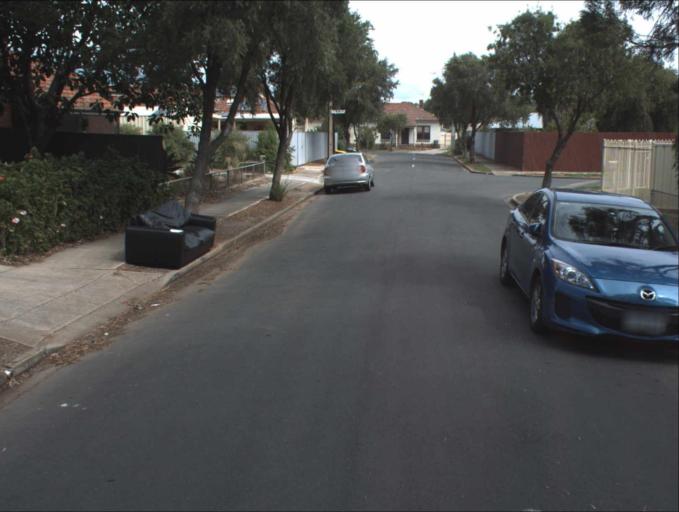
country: AU
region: South Australia
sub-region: Port Adelaide Enfield
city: Blair Athol
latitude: -34.8585
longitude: 138.5804
